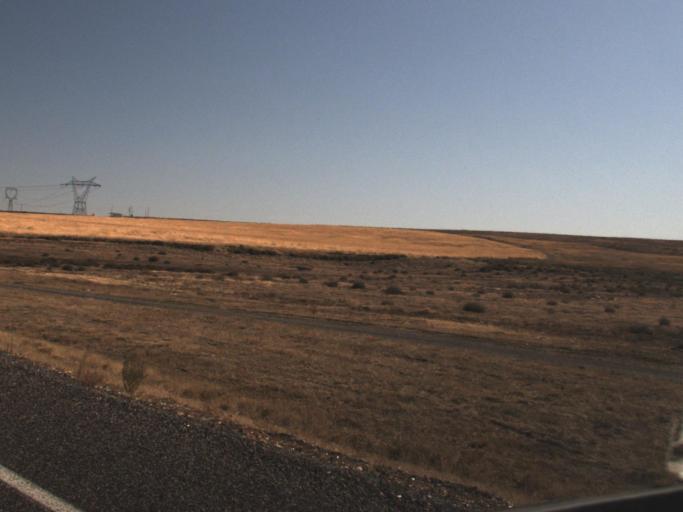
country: US
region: Washington
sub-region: Walla Walla County
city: Burbank
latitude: 46.2151
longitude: -118.8780
